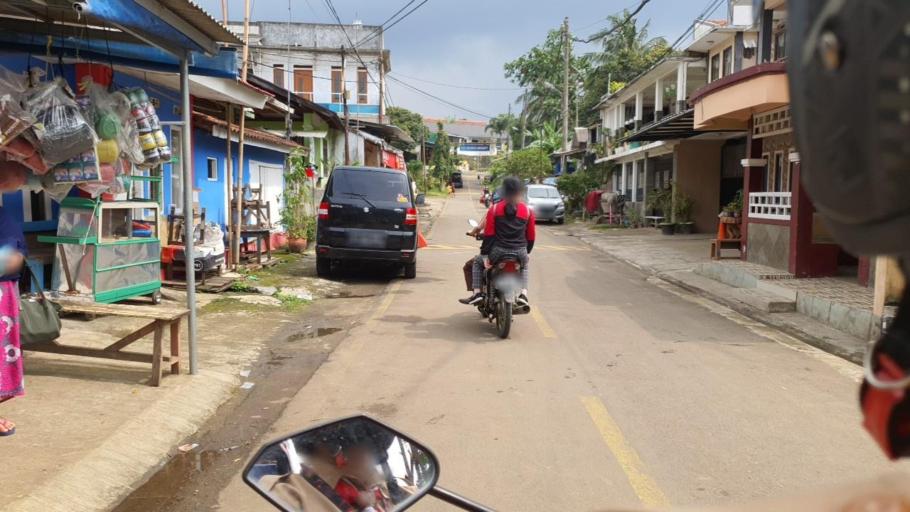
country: ID
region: West Java
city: Caringin
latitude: -6.6550
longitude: 106.8773
